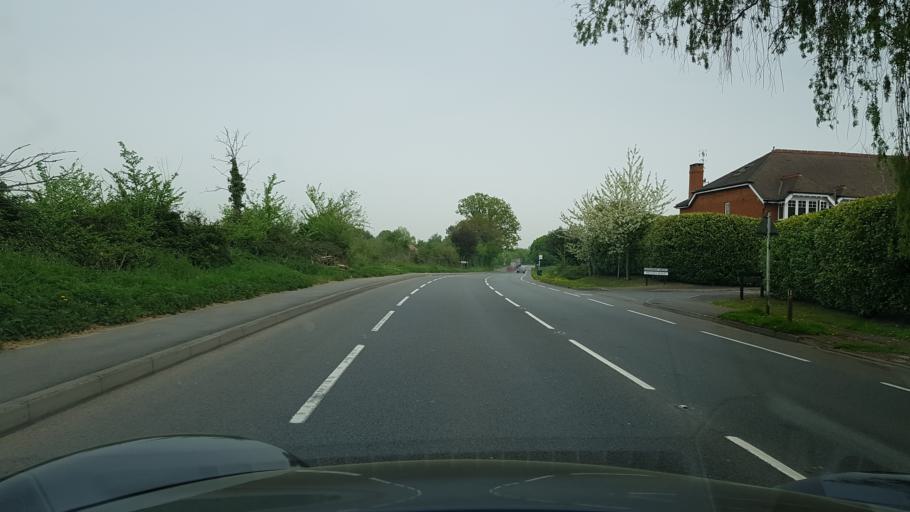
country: GB
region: England
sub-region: Surrey
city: Ripley
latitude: 51.2950
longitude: -0.5014
